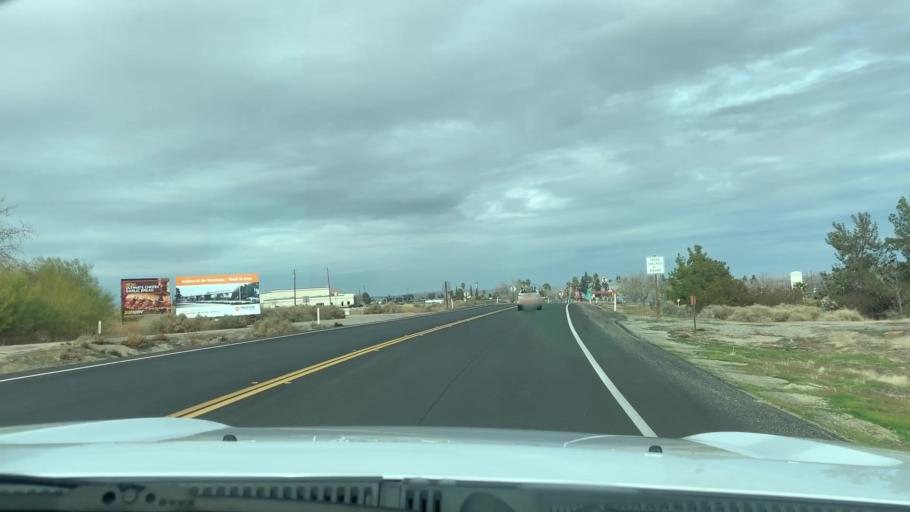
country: US
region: California
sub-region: Kern County
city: South Taft
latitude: 35.1333
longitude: -119.4470
